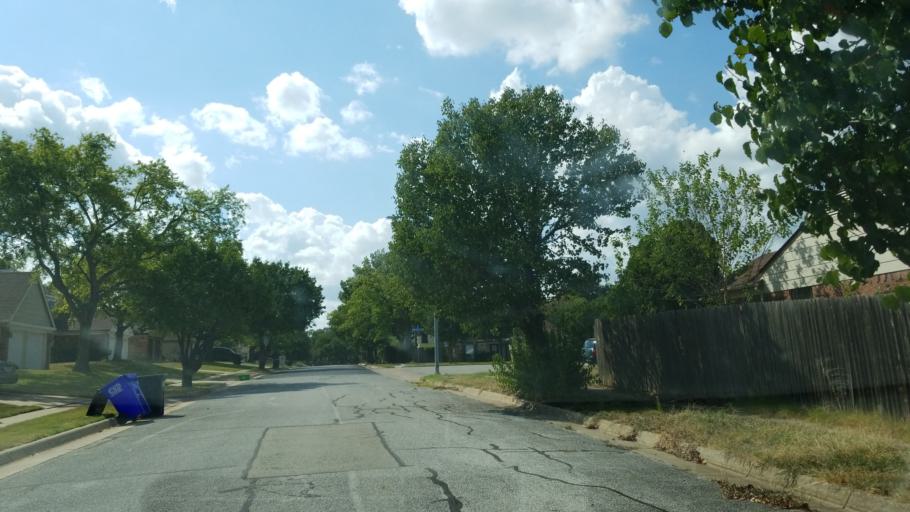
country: US
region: Texas
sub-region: Tarrant County
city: Euless
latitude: 32.8613
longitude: -97.0804
